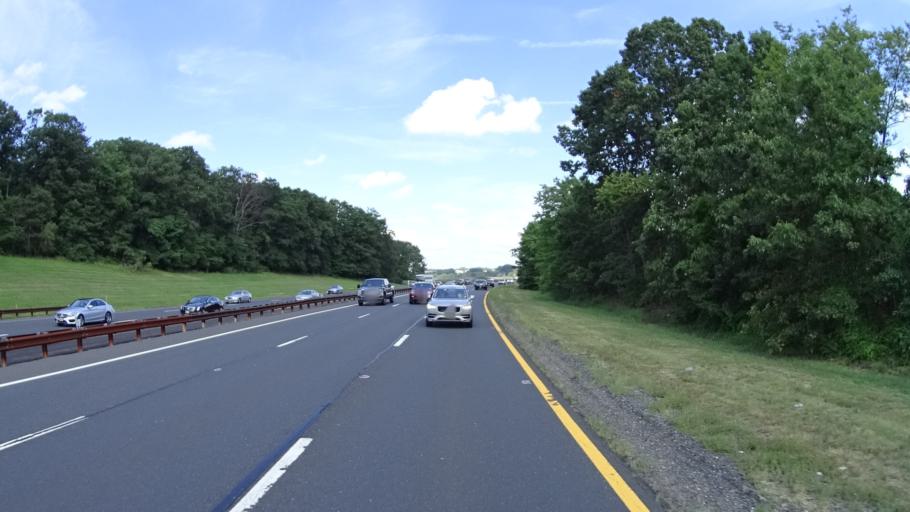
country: US
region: New Jersey
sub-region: Middlesex County
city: Laurence Harbor
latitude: 40.4437
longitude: -74.2666
